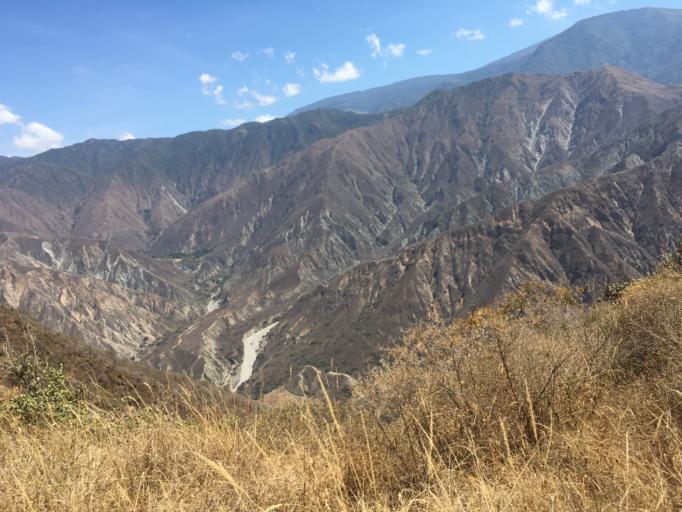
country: CO
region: Santander
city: Aratoca
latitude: 6.7960
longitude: -72.9939
